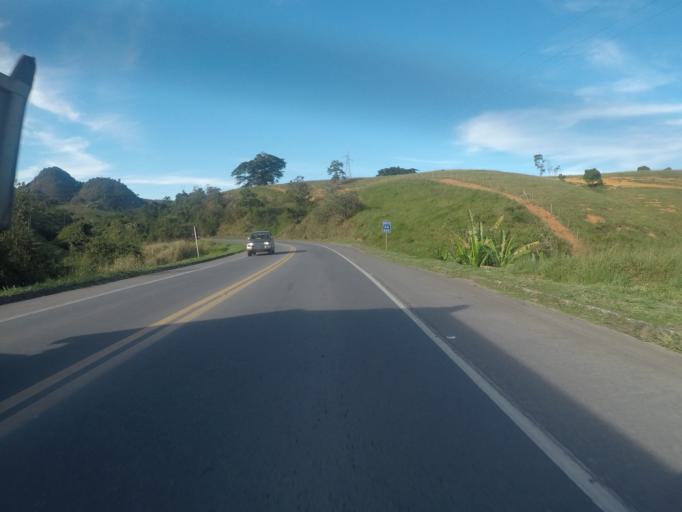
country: BR
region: Espirito Santo
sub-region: Ibiracu
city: Ibiracu
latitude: -19.8704
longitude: -40.4103
